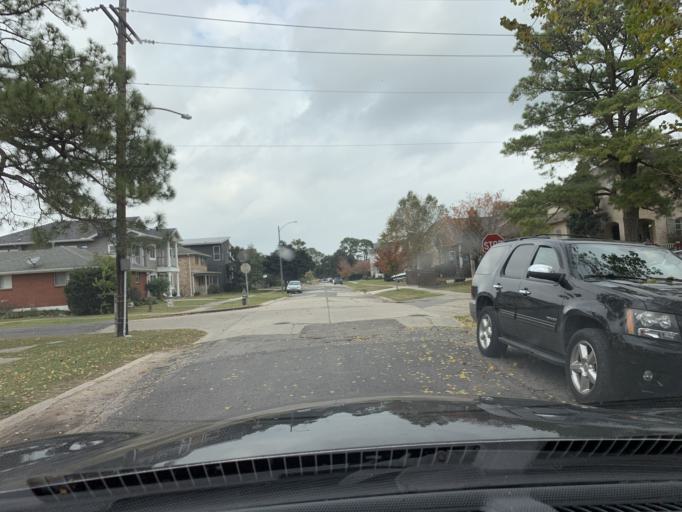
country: US
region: Louisiana
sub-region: Jefferson Parish
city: Metairie
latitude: 30.0098
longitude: -90.1031
